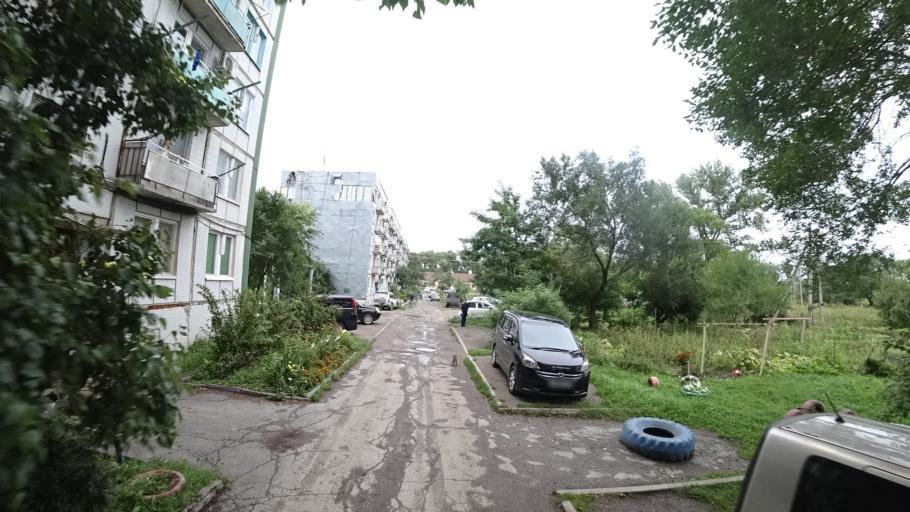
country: RU
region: Primorskiy
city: Chernigovka
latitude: 44.3300
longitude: 132.5321
